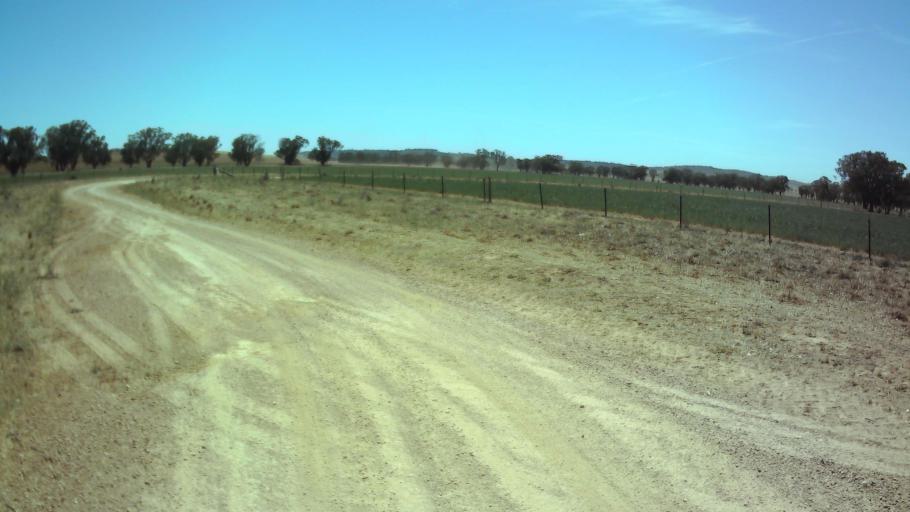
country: AU
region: New South Wales
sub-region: Weddin
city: Grenfell
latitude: -33.9929
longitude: 148.1569
